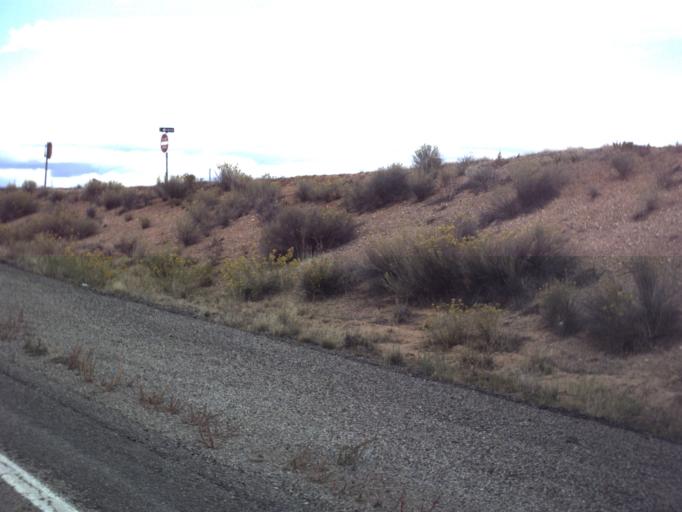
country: US
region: Colorado
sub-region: Mesa County
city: Loma
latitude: 39.0381
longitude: -109.2843
